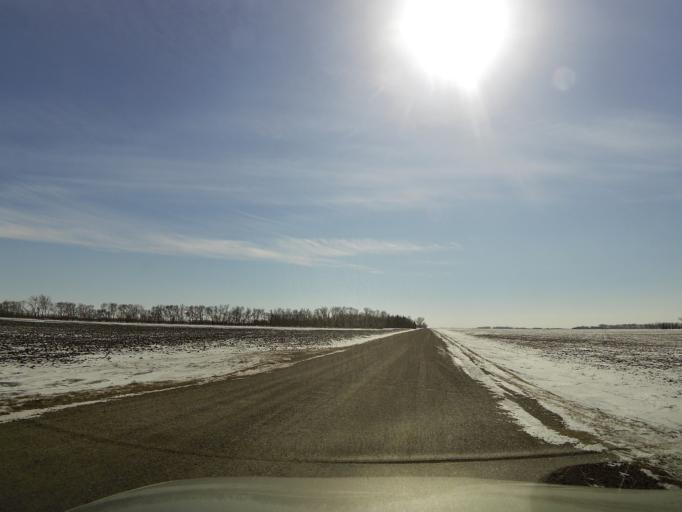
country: US
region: North Dakota
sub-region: Walsh County
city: Grafton
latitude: 48.4114
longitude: -97.2131
